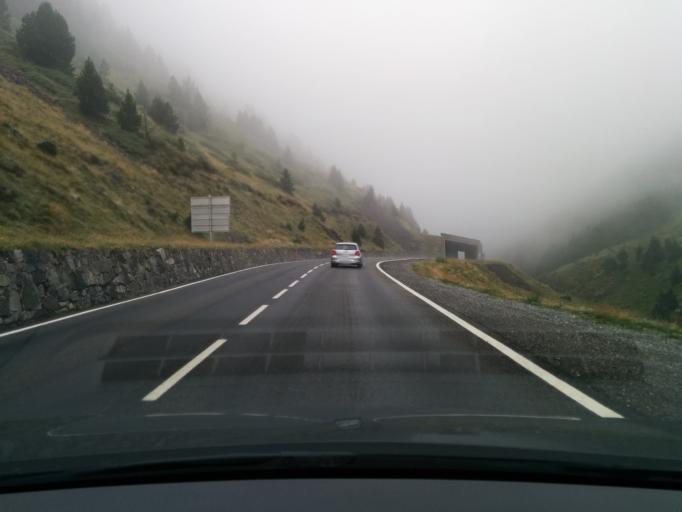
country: ES
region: Aragon
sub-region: Provincia de Huesca
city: Bielsa
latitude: 42.7602
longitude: 0.1961
